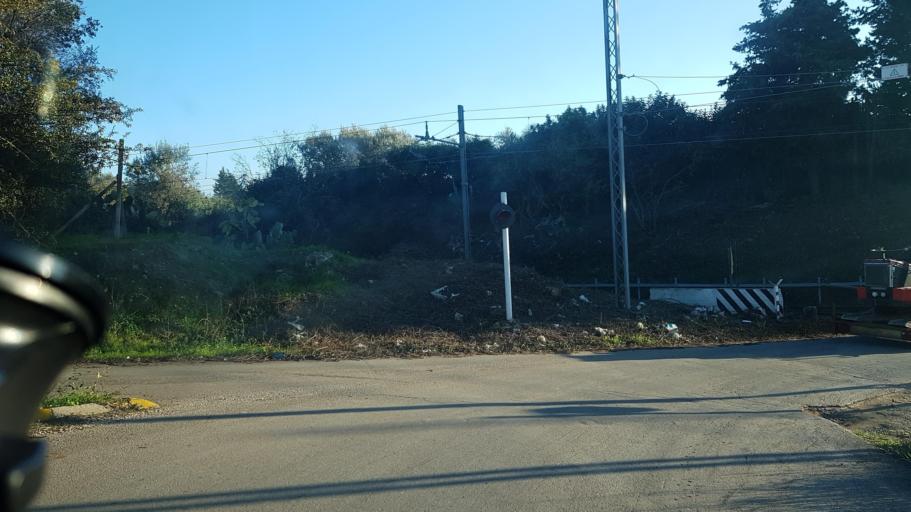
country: IT
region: Apulia
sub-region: Provincia di Brindisi
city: Latiano
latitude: 40.5593
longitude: 17.7350
